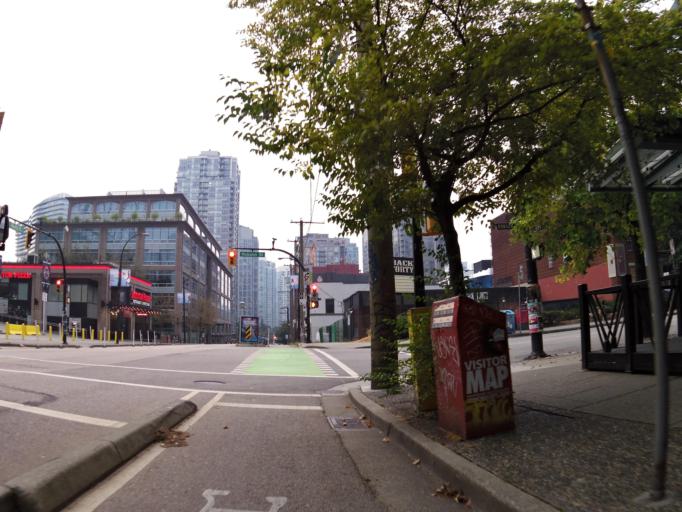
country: CA
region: British Columbia
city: West End
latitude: 49.2777
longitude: -123.1140
